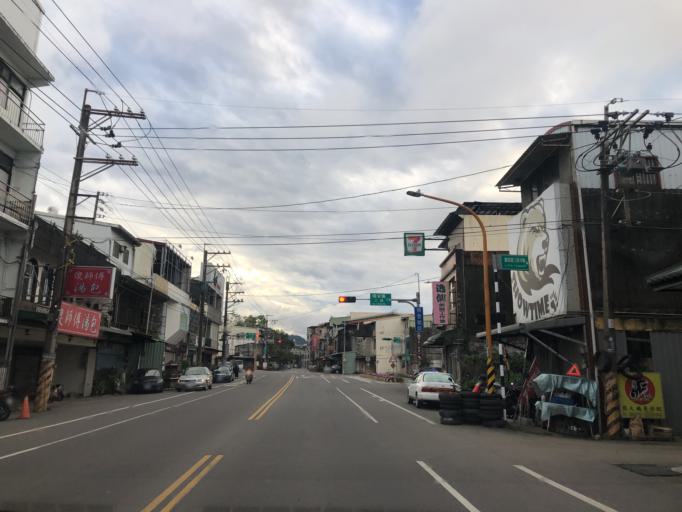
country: TW
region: Taiwan
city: Daxi
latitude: 24.8618
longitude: 121.2828
